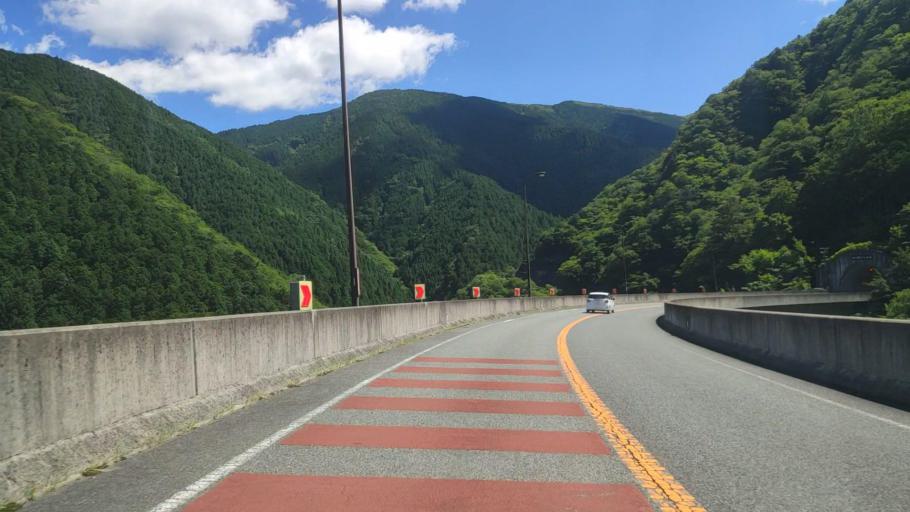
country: JP
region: Nara
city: Yoshino-cho
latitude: 34.2500
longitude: 135.9997
